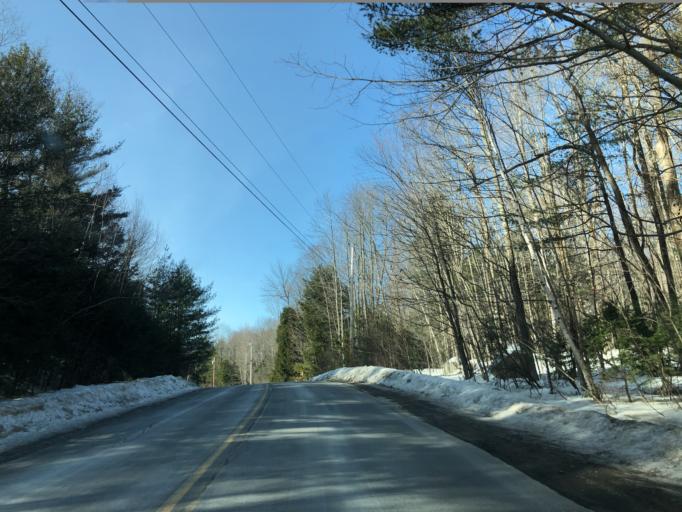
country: US
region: Maine
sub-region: Androscoggin County
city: Minot
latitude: 44.1428
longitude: -70.3239
